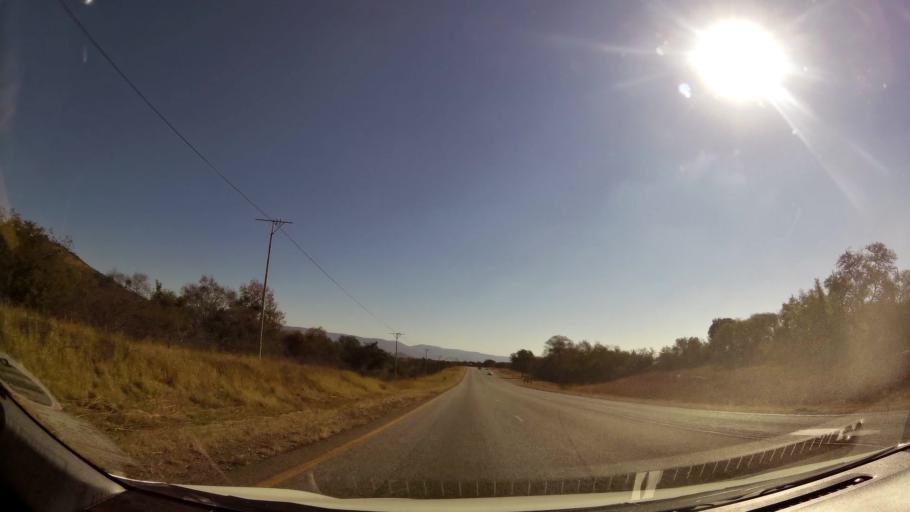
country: ZA
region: Limpopo
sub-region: Waterberg District Municipality
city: Mokopane
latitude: -24.1616
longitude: 29.0507
